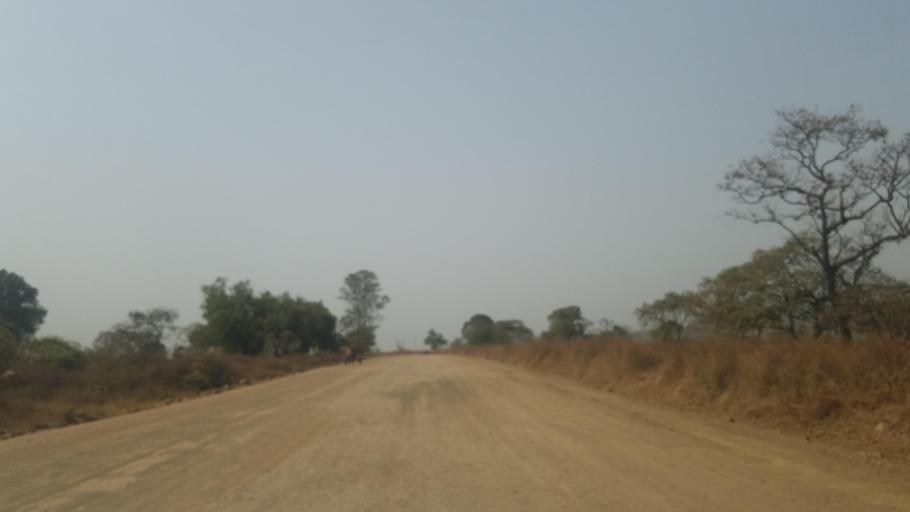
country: ET
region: Amhara
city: Bure
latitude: 10.9322
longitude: 36.4674
